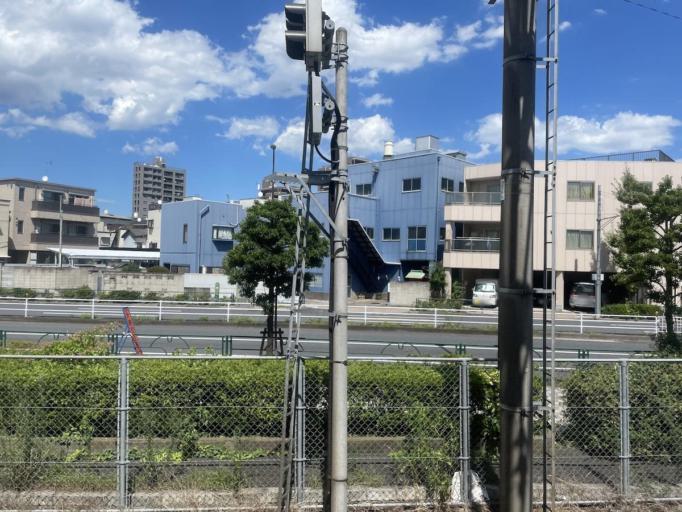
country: JP
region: Tokyo
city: Urayasu
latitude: 35.7086
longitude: 139.8309
